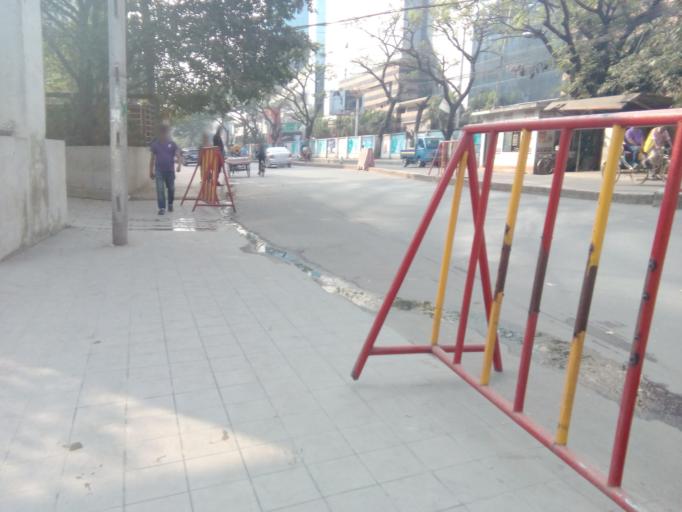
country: BD
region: Dhaka
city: Paltan
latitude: 23.8126
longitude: 90.4253
